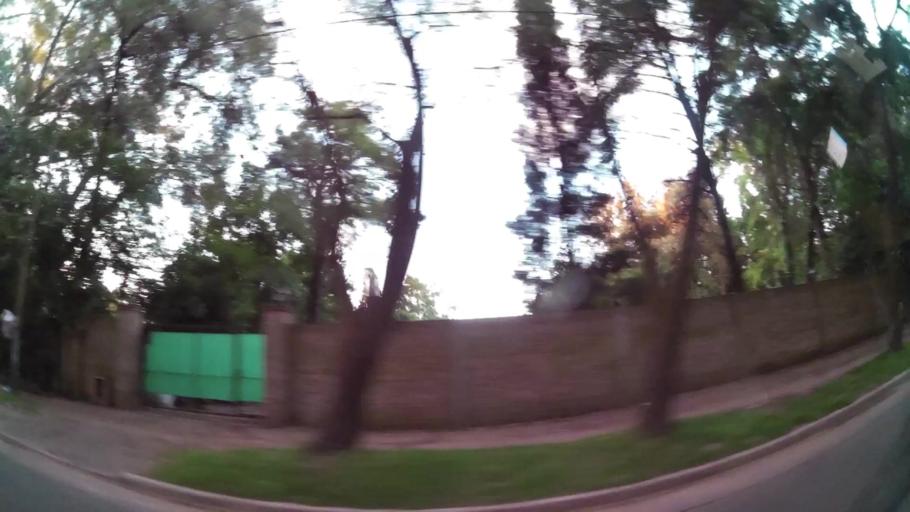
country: AR
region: Buenos Aires
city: Santa Catalina - Dique Lujan
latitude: -34.4809
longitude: -58.7745
